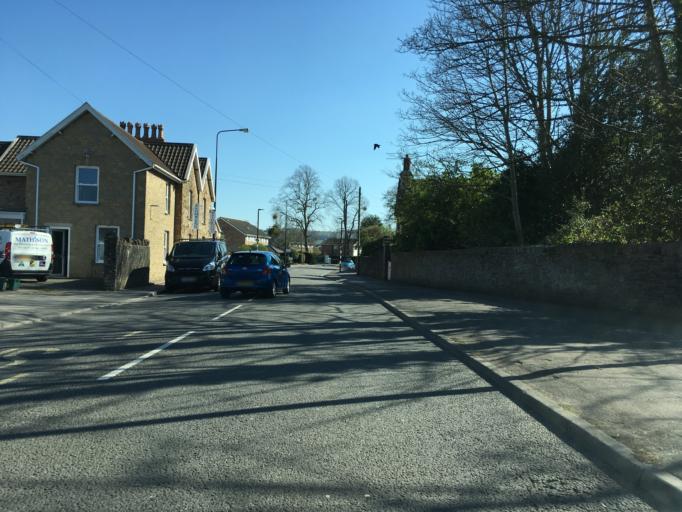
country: GB
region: England
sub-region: North Somerset
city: Portishead
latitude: 51.4796
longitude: -2.7681
